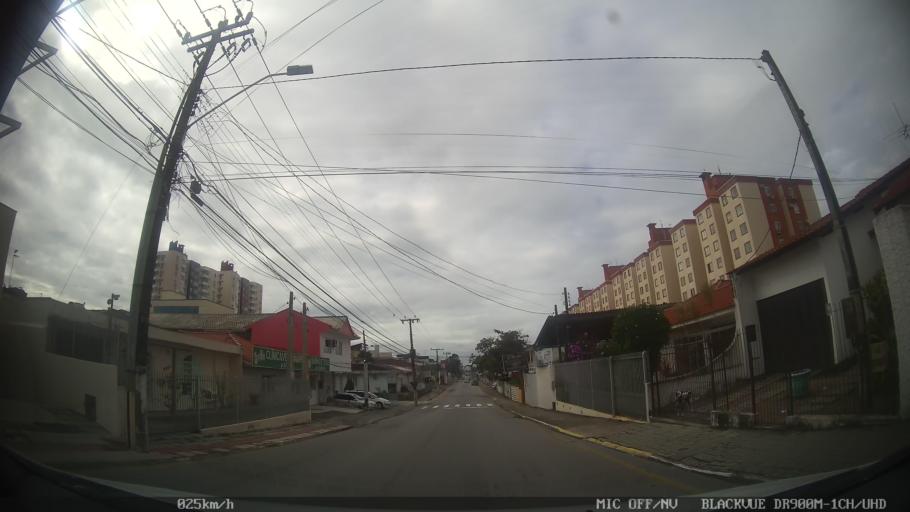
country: BR
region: Santa Catarina
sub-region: Sao Jose
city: Campinas
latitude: -27.5635
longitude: -48.6231
